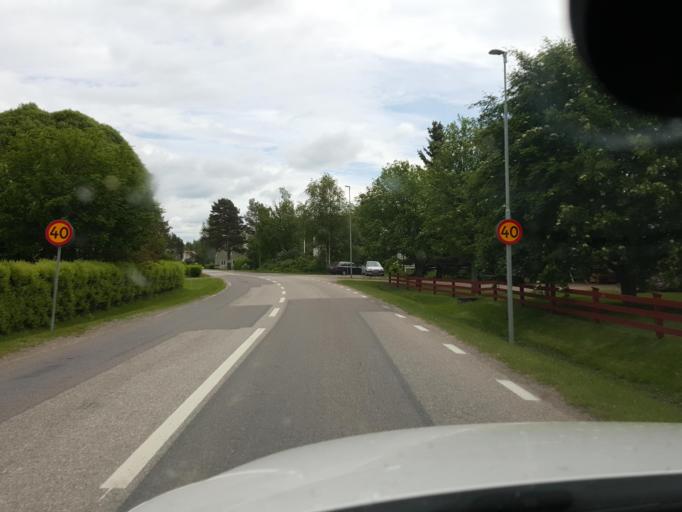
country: SE
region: Gaevleborg
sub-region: Ljusdals Kommun
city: Farila
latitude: 61.8114
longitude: 15.7496
